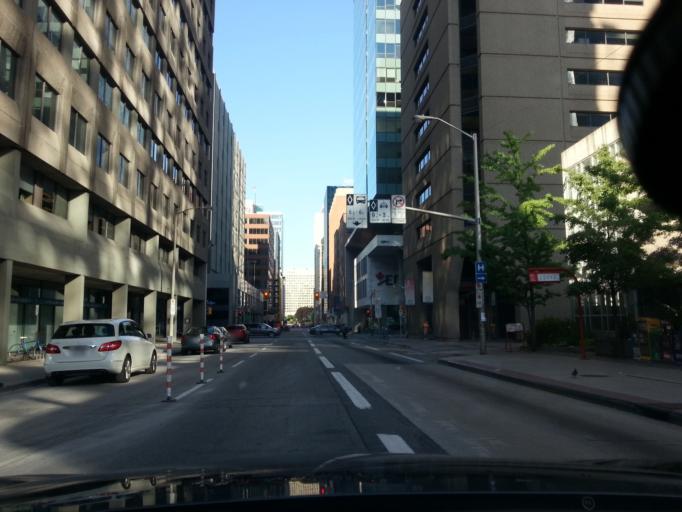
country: CA
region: Ontario
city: Ottawa
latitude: 45.4199
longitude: -75.6986
